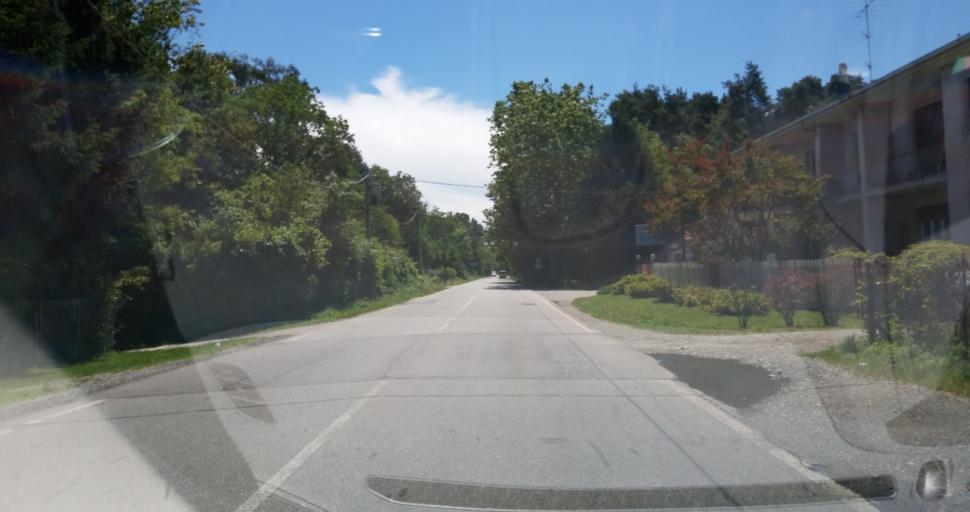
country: IT
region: Lombardy
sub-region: Provincia di Varese
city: Vergiate
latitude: 45.7105
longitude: 8.6955
